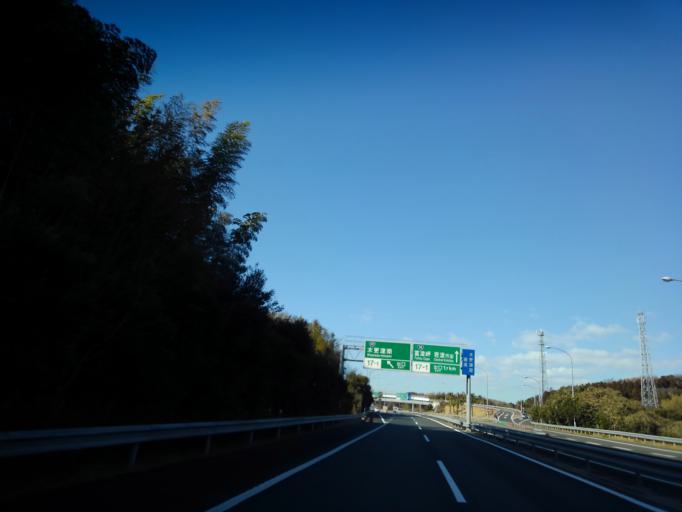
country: JP
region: Chiba
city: Kisarazu
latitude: 35.3502
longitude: 139.9246
